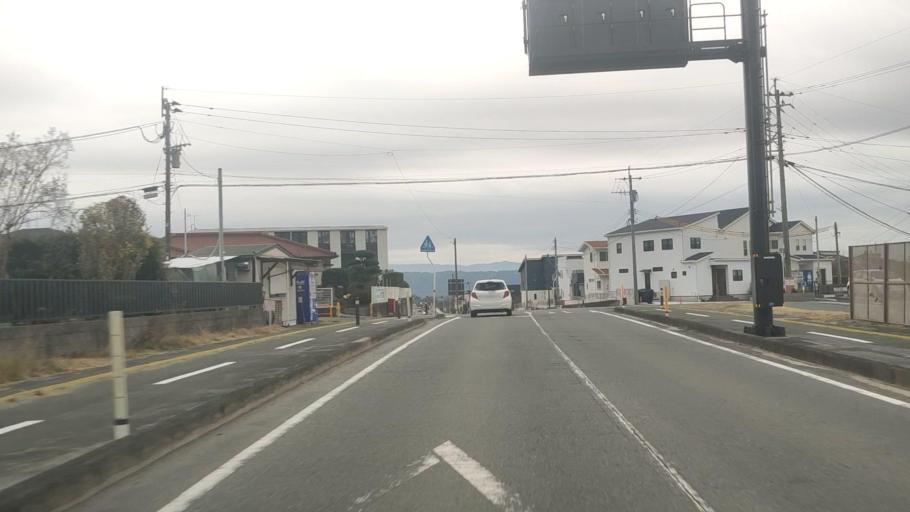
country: JP
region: Kumamoto
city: Ozu
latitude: 32.8790
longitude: 130.8939
